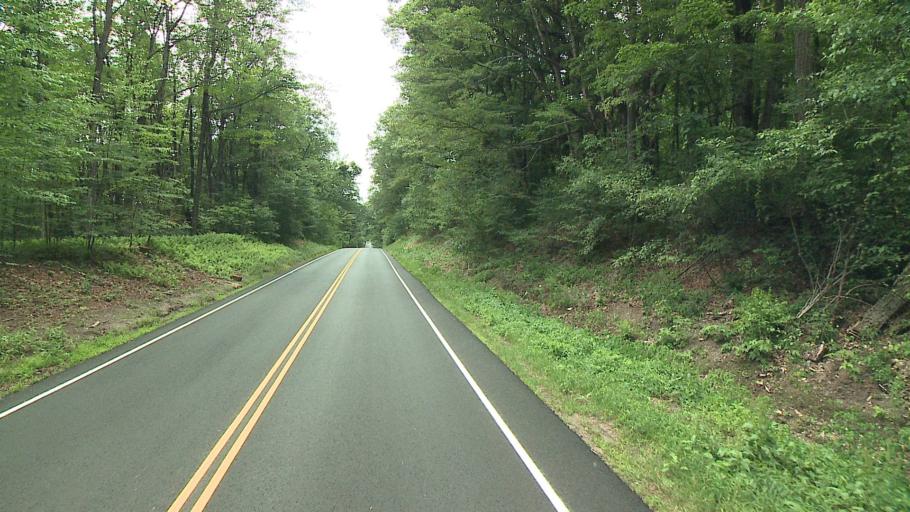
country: US
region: Massachusetts
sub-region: Hampden County
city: Granville
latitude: 42.0228
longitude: -72.8887
